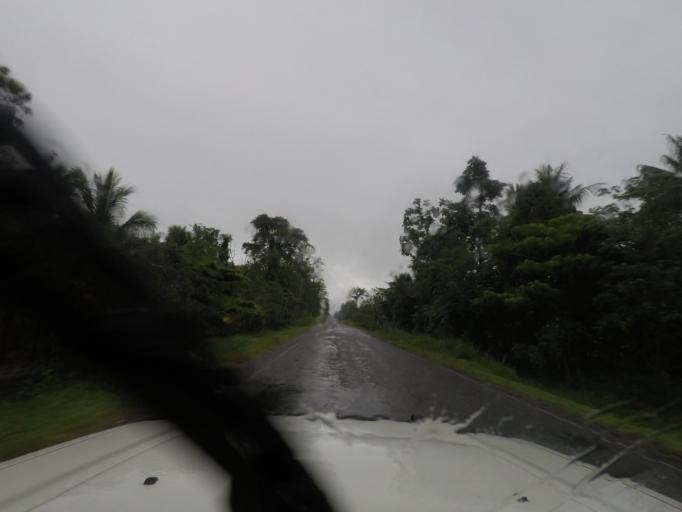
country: PG
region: Madang
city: Madang
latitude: -5.3882
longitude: 145.6864
